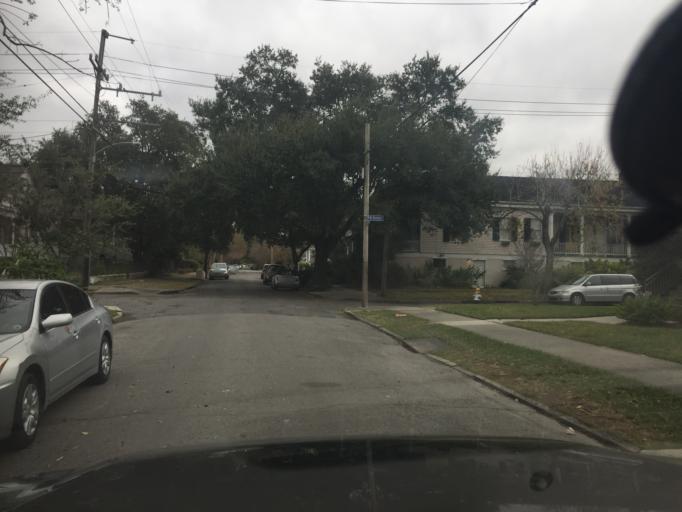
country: US
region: Louisiana
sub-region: Orleans Parish
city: New Orleans
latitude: 29.9789
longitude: -90.0852
